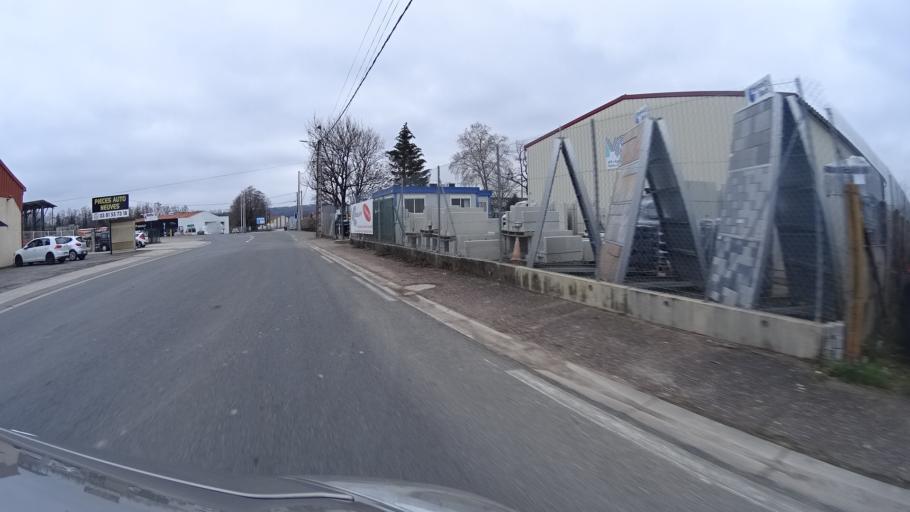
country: FR
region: Franche-Comte
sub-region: Departement du Doubs
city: Saone
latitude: 47.2115
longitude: 6.0998
